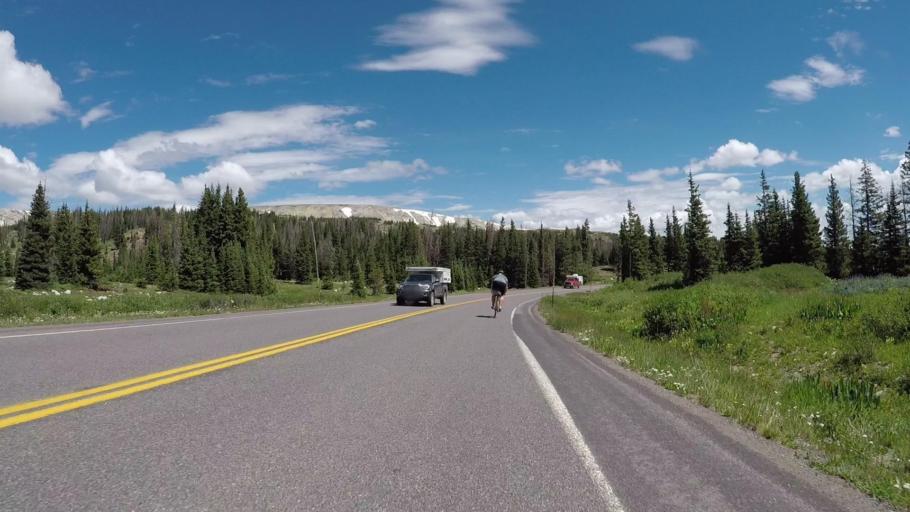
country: US
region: Wyoming
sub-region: Carbon County
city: Saratoga
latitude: 41.3496
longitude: -106.2882
